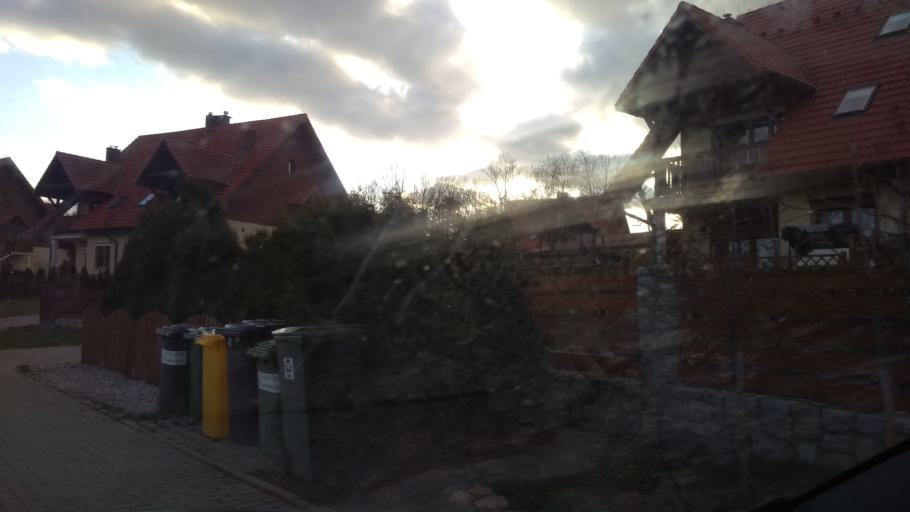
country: PL
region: Lower Silesian Voivodeship
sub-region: Jelenia Gora
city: Cieplice Slaskie Zdroj
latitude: 50.8546
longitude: 15.7154
